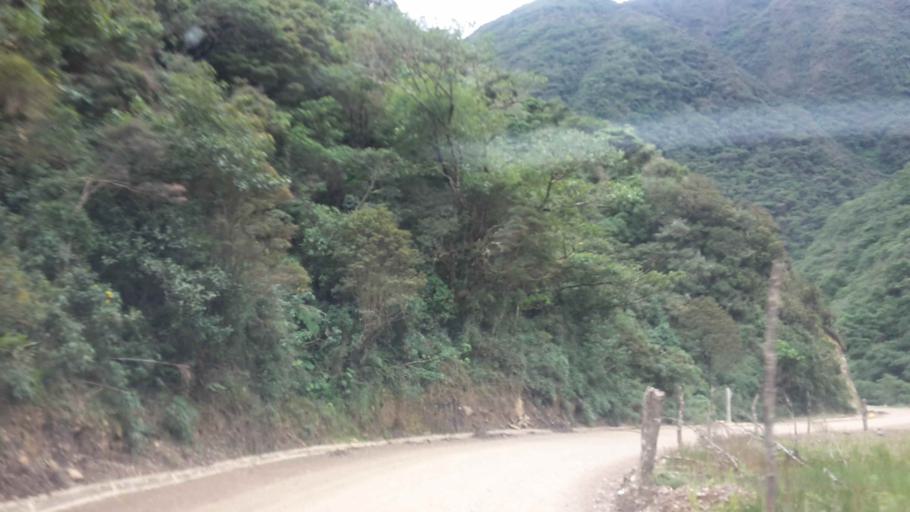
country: BO
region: Cochabamba
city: Totora
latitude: -17.5600
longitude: -65.2720
